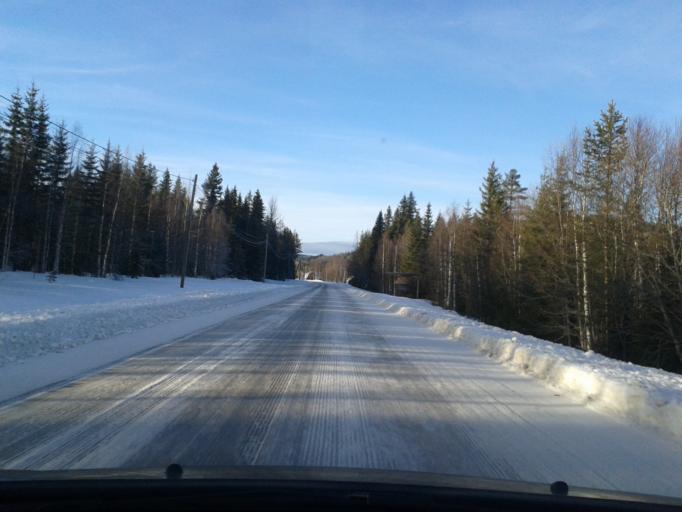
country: SE
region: Vaesterbotten
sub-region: Asele Kommun
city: Asele
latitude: 63.7809
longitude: 17.6632
